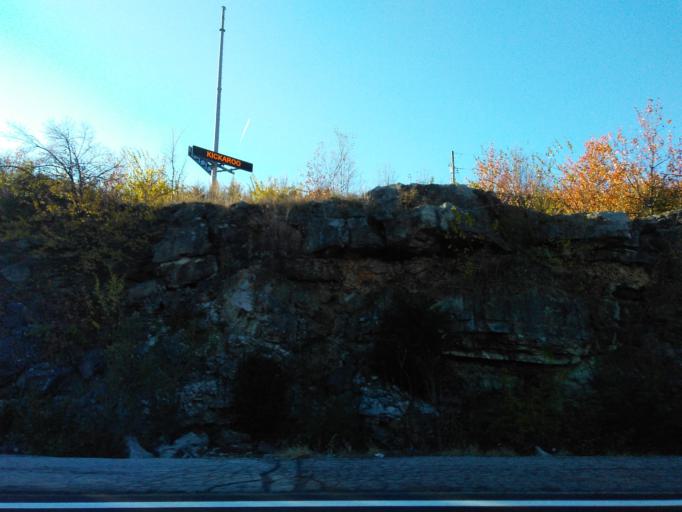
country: US
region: Missouri
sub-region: Saint Louis County
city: Concord
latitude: 38.5124
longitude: -90.3701
